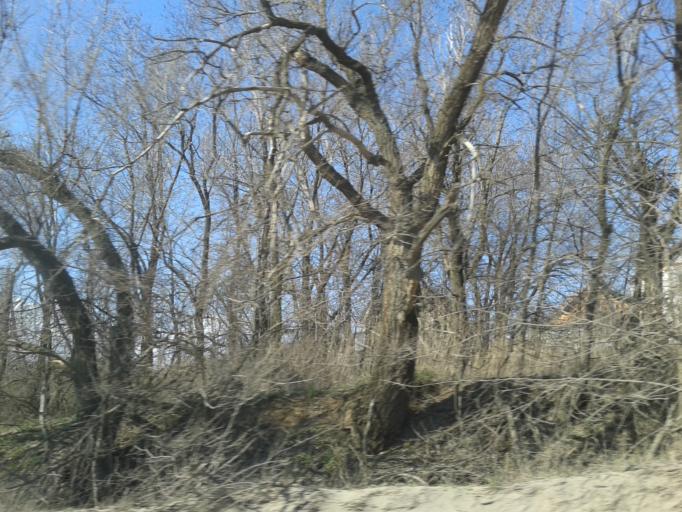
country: RU
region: Volgograd
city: Volgograd
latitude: 48.6301
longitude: 44.3991
